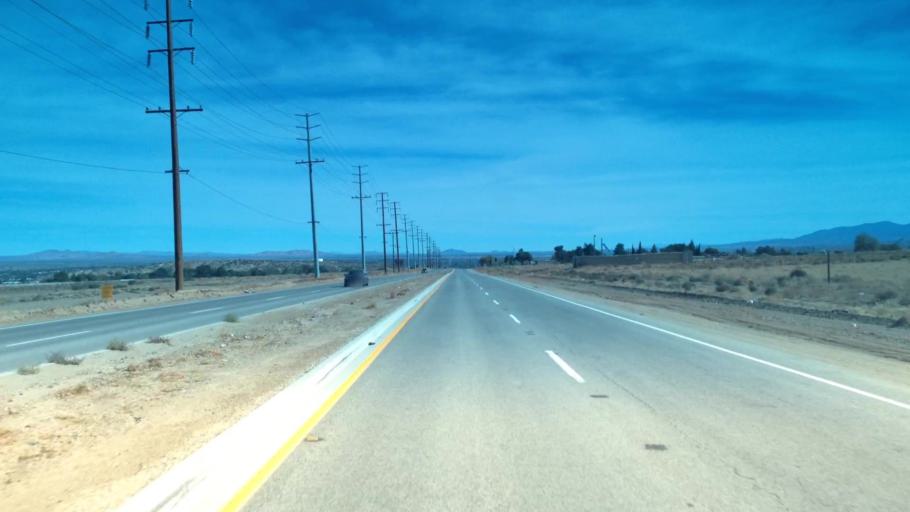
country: US
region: California
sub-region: Los Angeles County
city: Desert View Highlands
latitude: 34.5581
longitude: -118.1578
